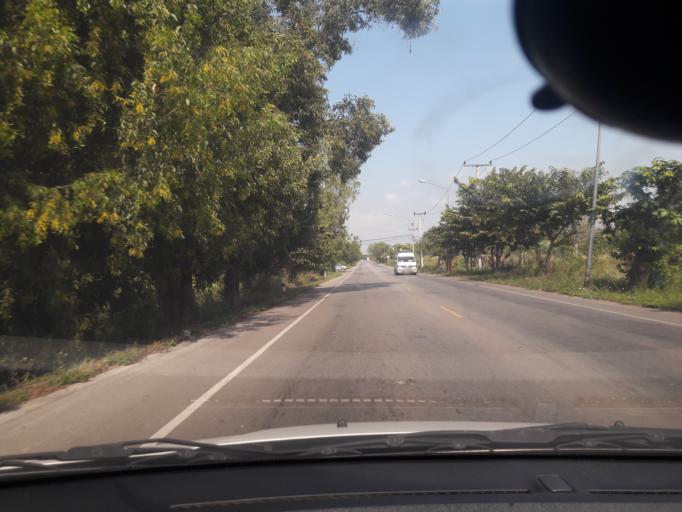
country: TH
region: Lampang
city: Mae Tha
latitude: 18.2114
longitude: 99.4939
